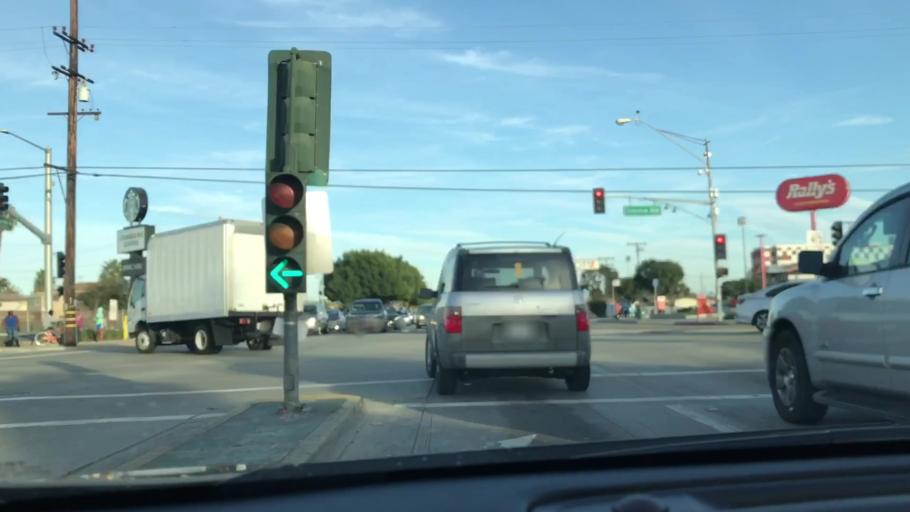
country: US
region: California
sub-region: Los Angeles County
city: Alondra Park
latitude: 33.9019
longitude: -118.3268
